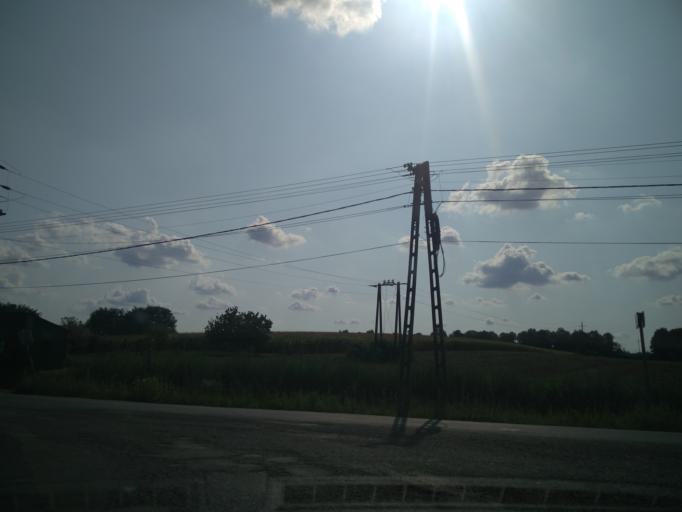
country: HU
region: Zala
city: Zalaegerszeg
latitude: 46.8836
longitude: 16.7517
